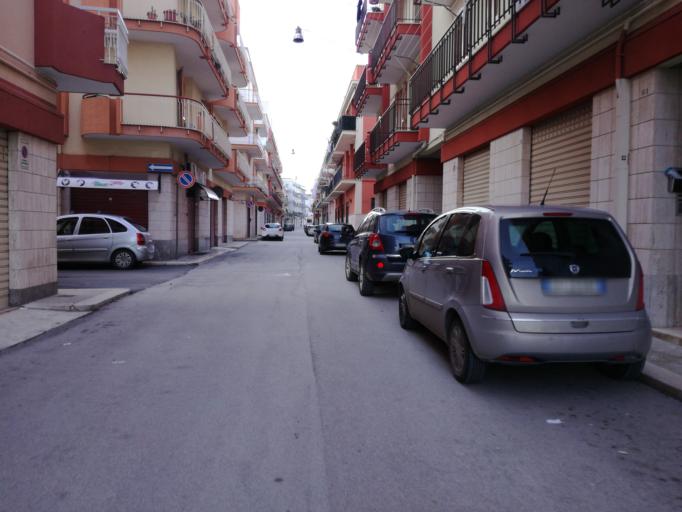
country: IT
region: Apulia
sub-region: Provincia di Bari
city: Corato
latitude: 41.1481
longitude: 16.4168
